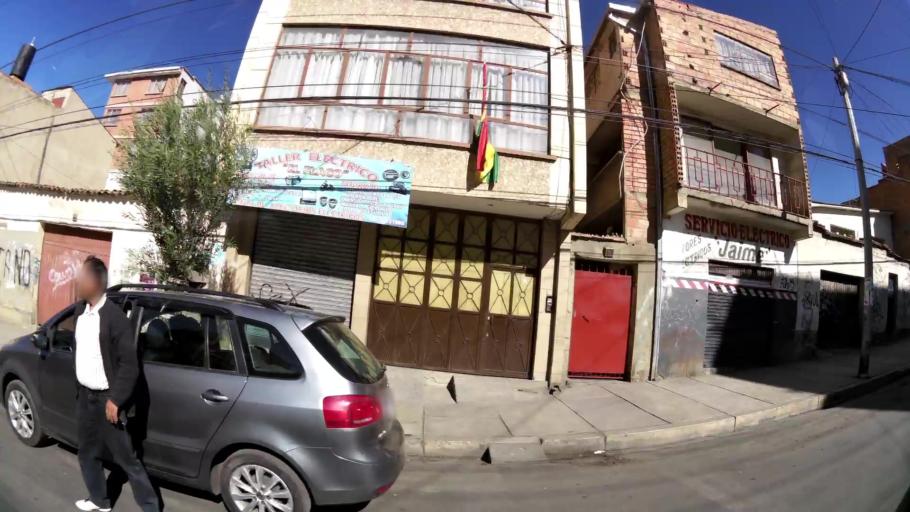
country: BO
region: La Paz
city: La Paz
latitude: -16.5105
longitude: -68.1373
